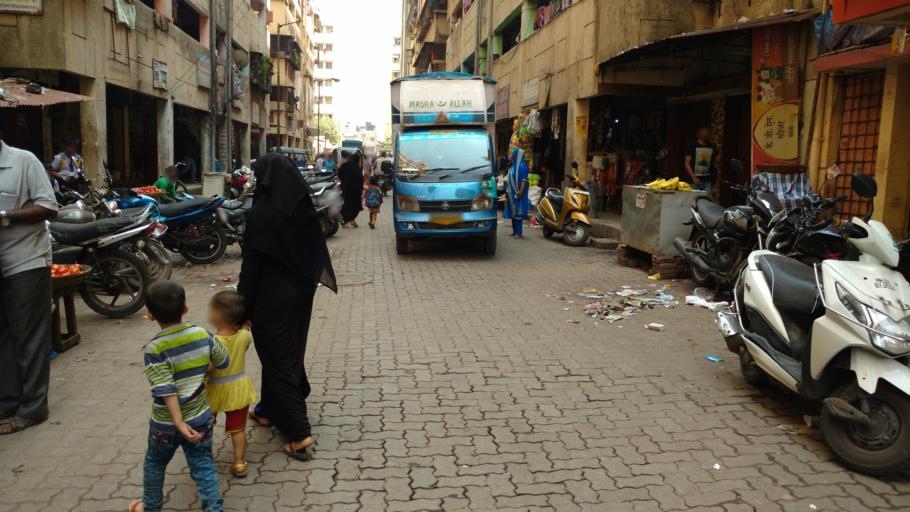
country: IN
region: Maharashtra
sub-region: Mumbai Suburban
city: Mumbai
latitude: 19.0647
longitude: 72.9158
